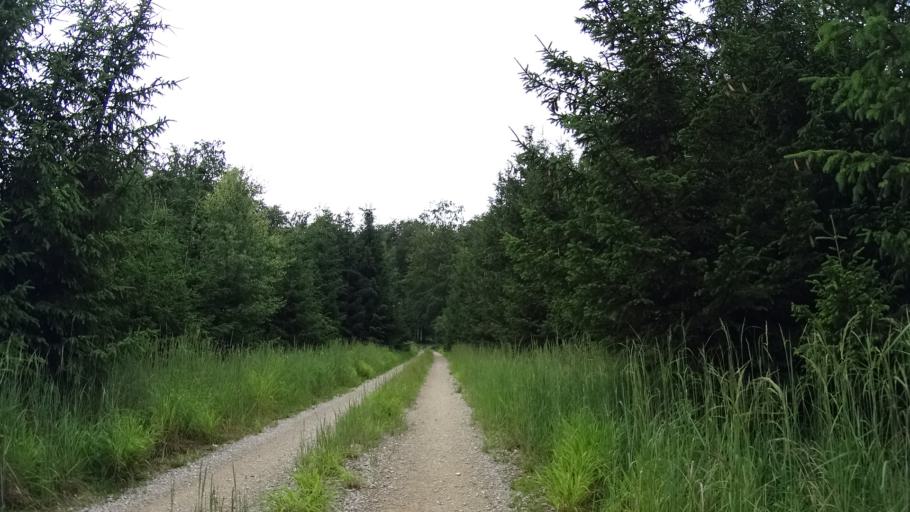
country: DE
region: Bavaria
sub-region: Upper Bavaria
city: Denkendorf
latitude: 48.9038
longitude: 11.4772
